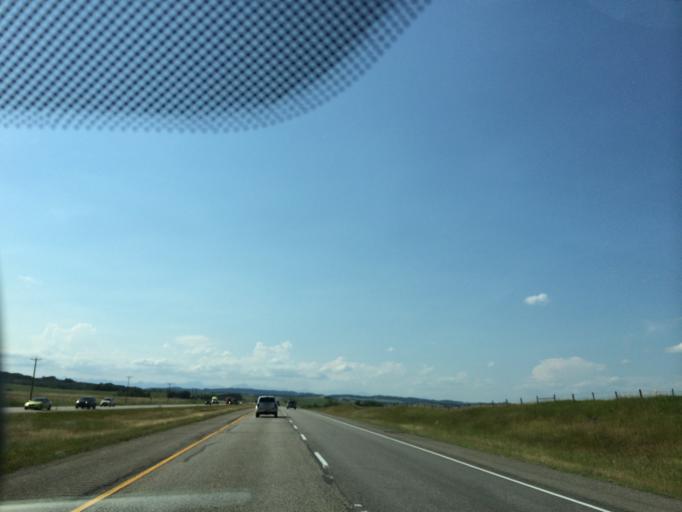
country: CA
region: Alberta
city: Cochrane
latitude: 51.1037
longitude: -114.6178
